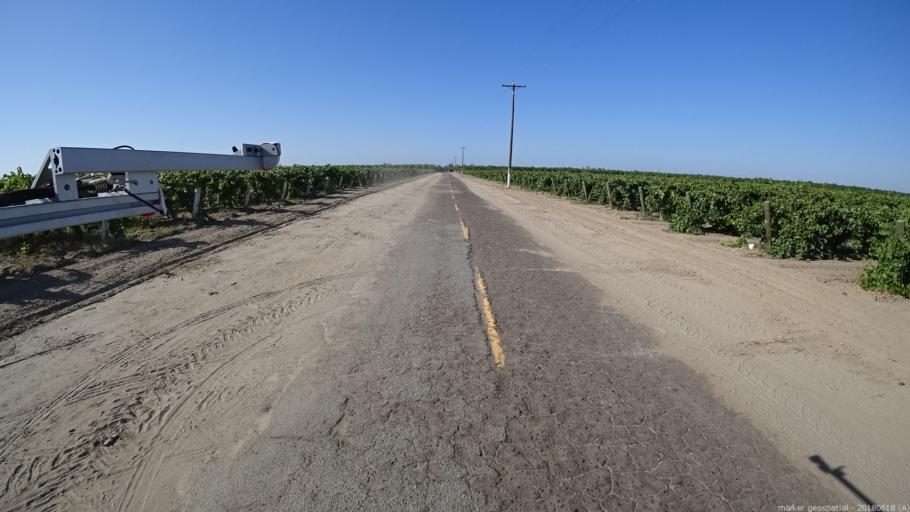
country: US
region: California
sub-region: Fresno County
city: Biola
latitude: 36.8252
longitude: -120.1059
